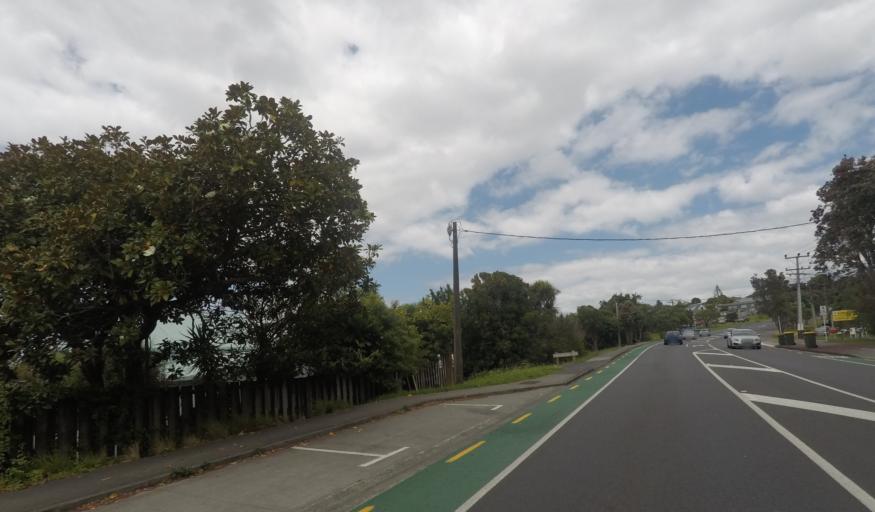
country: NZ
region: Auckland
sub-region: Auckland
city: Rosebank
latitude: -36.8273
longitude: 174.6078
